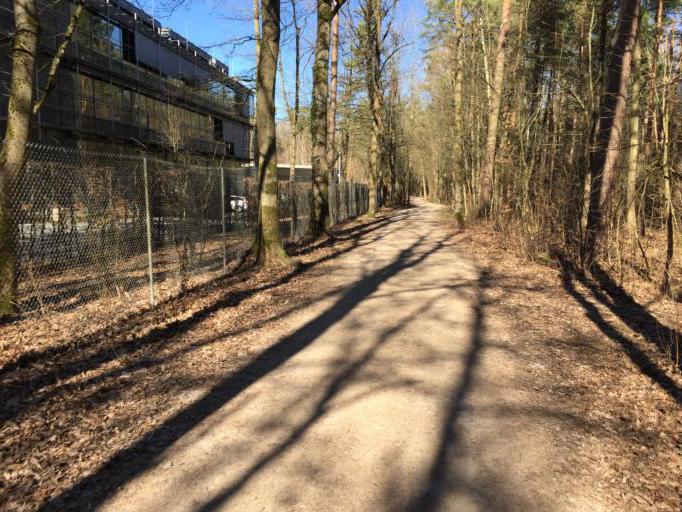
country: DE
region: Bavaria
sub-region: Regierungsbezirk Mittelfranken
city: Erlangen
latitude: 49.5661
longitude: 11.0078
